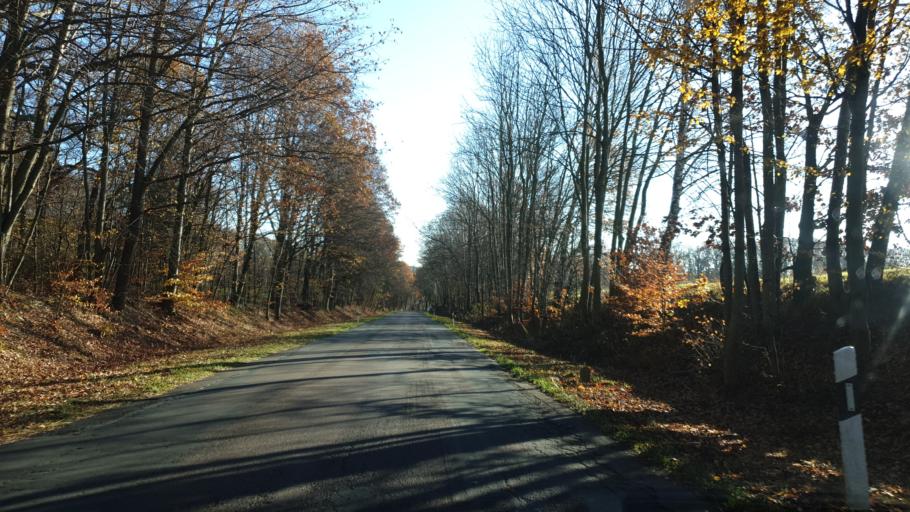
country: DE
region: Saxony-Anhalt
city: Wetterzeube
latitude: 51.0139
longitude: 12.0022
